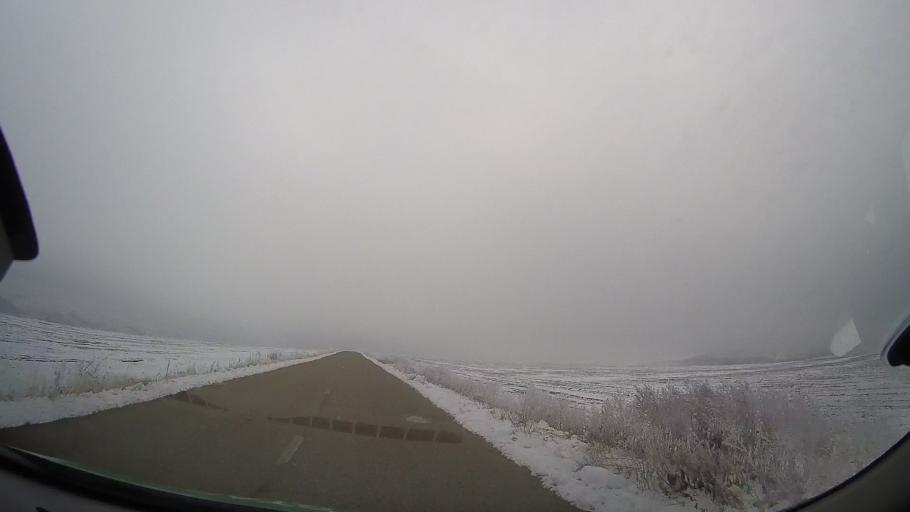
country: RO
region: Vaslui
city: Coroiesti
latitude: 46.2241
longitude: 27.4786
